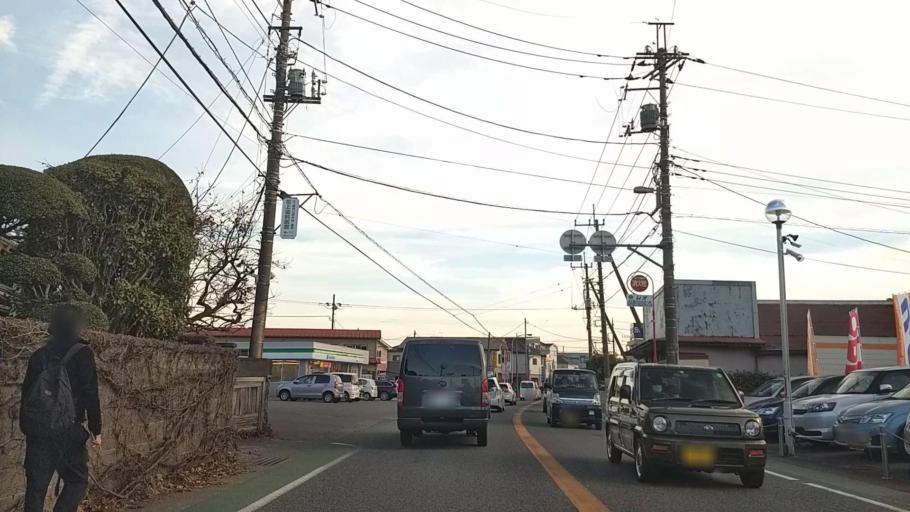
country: JP
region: Kanagawa
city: Atsugi
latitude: 35.4780
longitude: 139.3422
